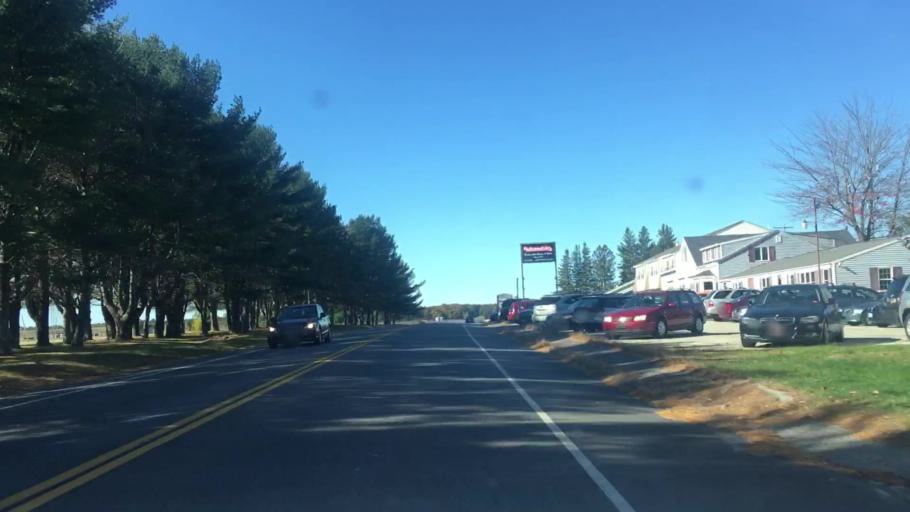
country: US
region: Maine
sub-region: Cumberland County
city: Brunswick
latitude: 43.9066
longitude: -69.9307
